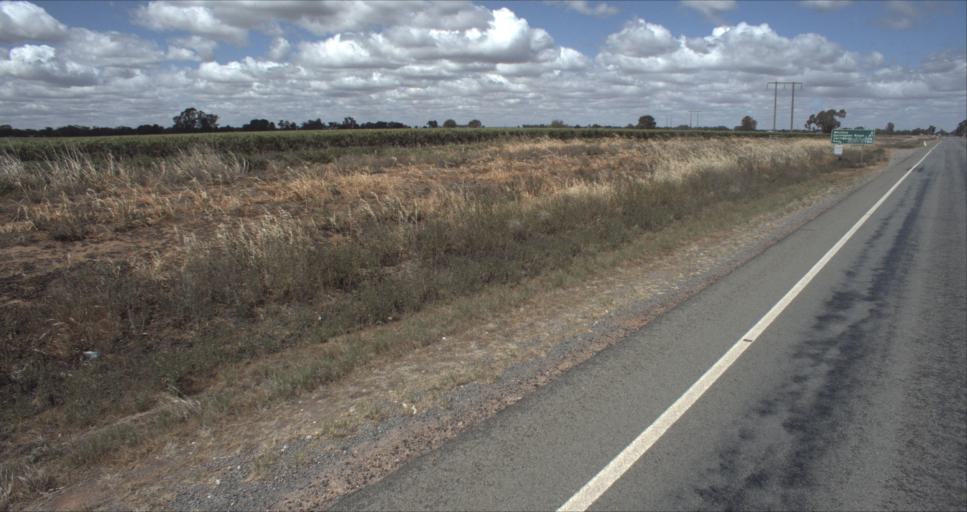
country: AU
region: New South Wales
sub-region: Murrumbidgee Shire
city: Darlington Point
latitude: -34.5056
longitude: 146.1873
